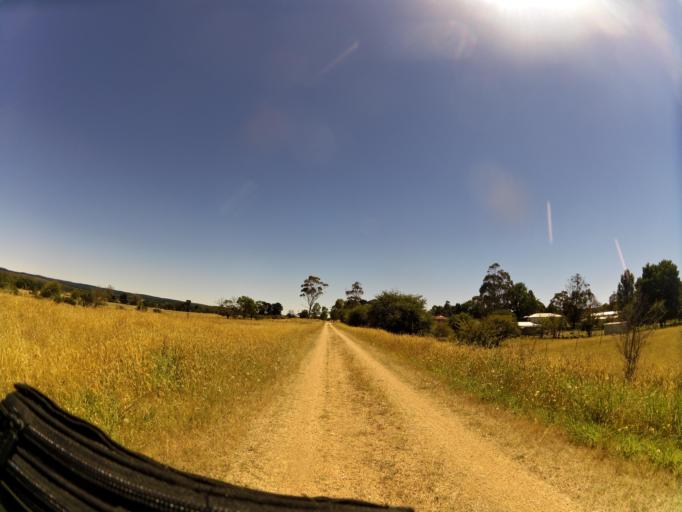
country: AU
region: Victoria
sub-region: Ballarat North
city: Delacombe
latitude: -37.6941
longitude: 143.6546
